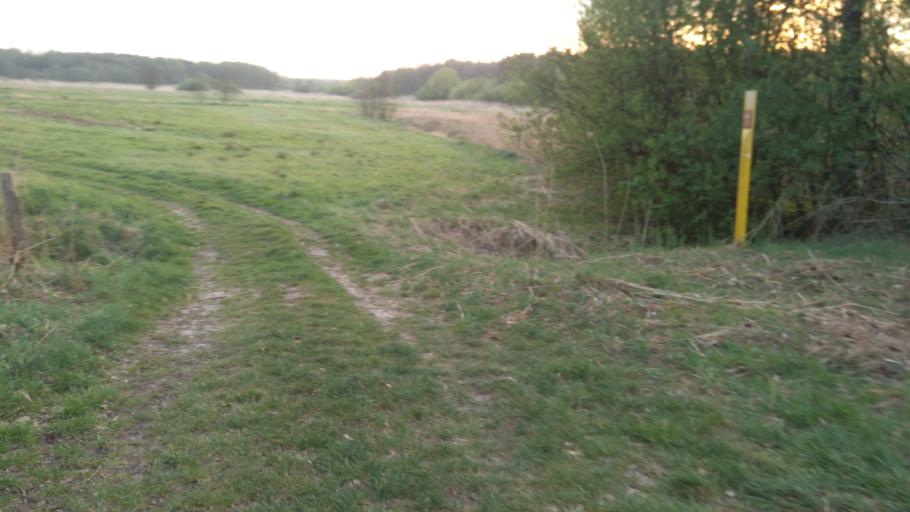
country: DE
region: Lower Saxony
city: Bliedersdorf
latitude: 53.4807
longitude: 9.5420
